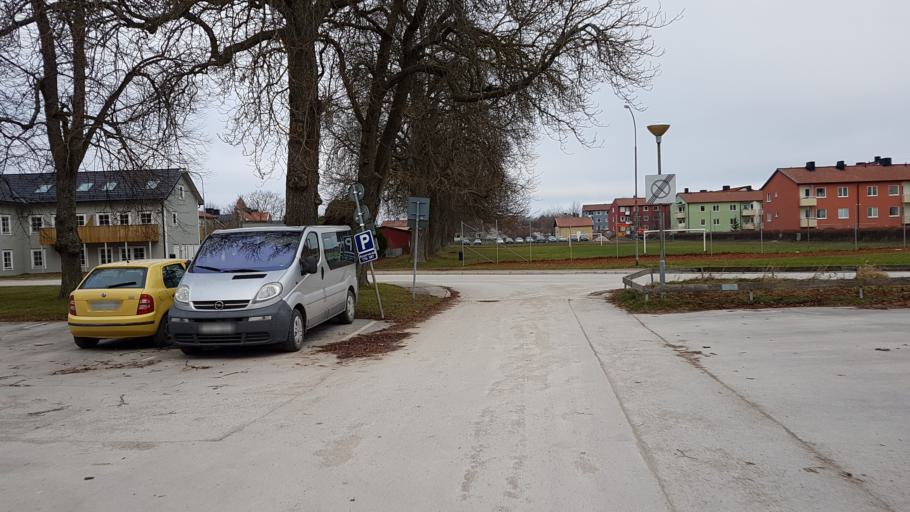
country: SE
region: Gotland
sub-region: Gotland
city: Visby
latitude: 57.6263
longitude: 18.2969
